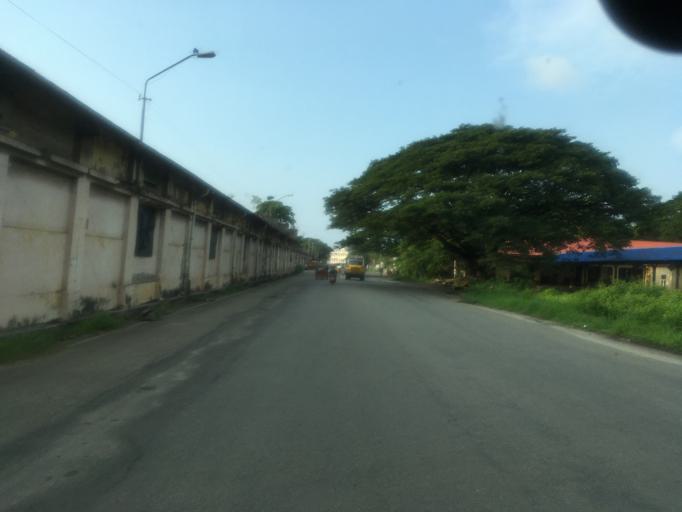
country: IN
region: Kerala
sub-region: Ernakulam
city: Cochin
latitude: 9.9594
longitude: 76.2675
